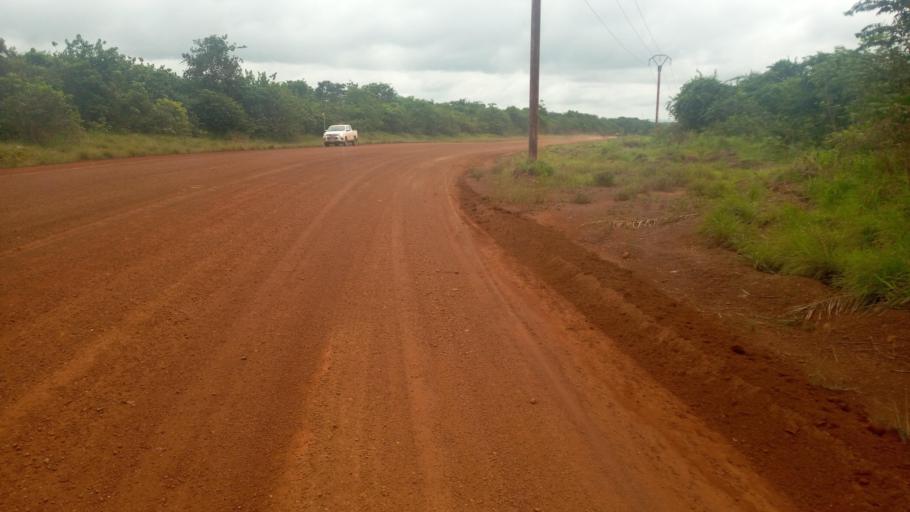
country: SL
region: Southern Province
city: Mogbwemo
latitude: 7.7222
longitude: -12.2852
